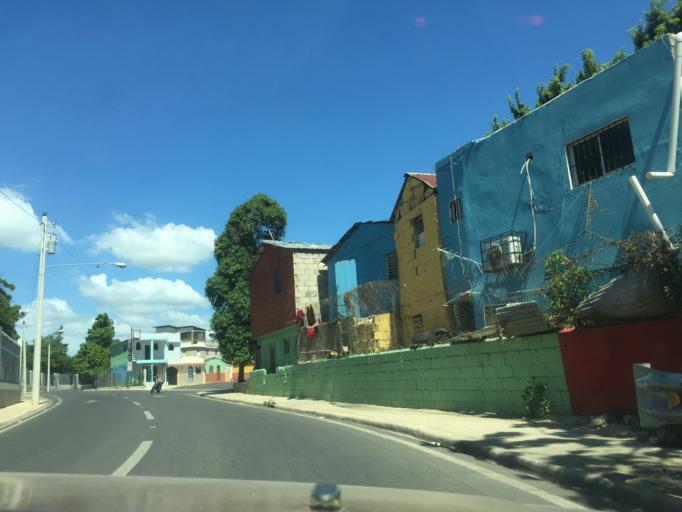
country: DO
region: Santiago
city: Santiago de los Caballeros
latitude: 19.4715
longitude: -70.7073
